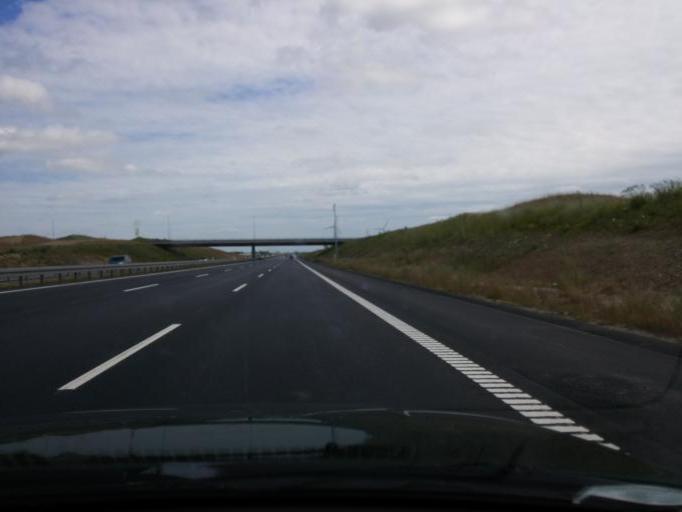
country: DK
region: South Denmark
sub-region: Middelfart Kommune
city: Strib
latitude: 55.4941
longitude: 9.8114
